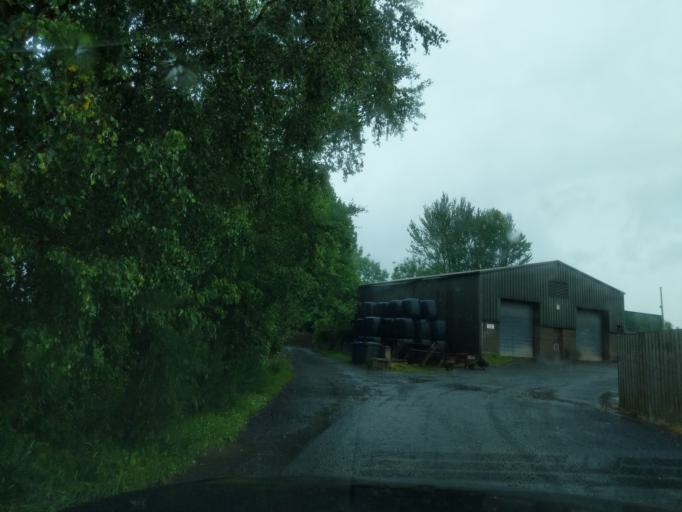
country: GB
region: Scotland
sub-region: Midlothian
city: Penicuik
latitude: 55.8453
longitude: -3.1888
